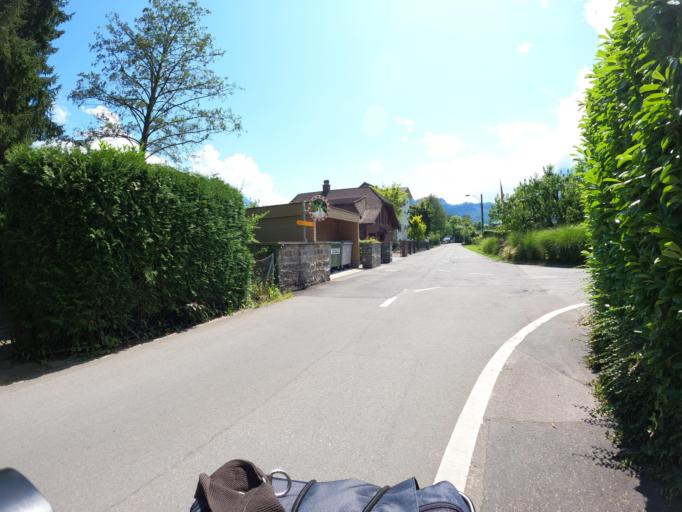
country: CH
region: Nidwalden
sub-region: Nidwalden
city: Stansstad
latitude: 47.0032
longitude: 8.3344
